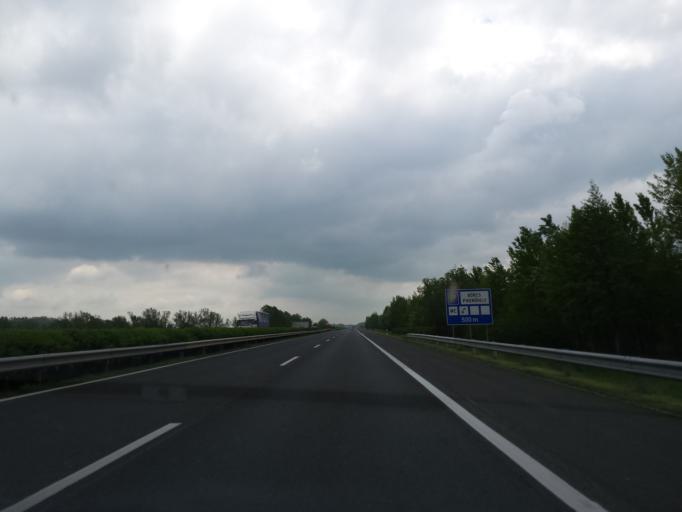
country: HU
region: Gyor-Moson-Sopron
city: Otteveny
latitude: 47.7126
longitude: 17.4776
